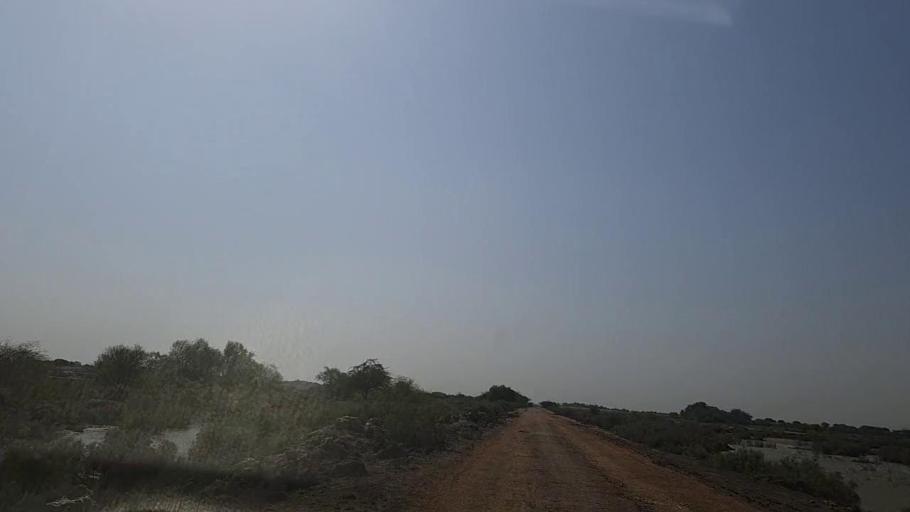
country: PK
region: Sindh
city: Daro Mehar
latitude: 24.7021
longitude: 68.1283
